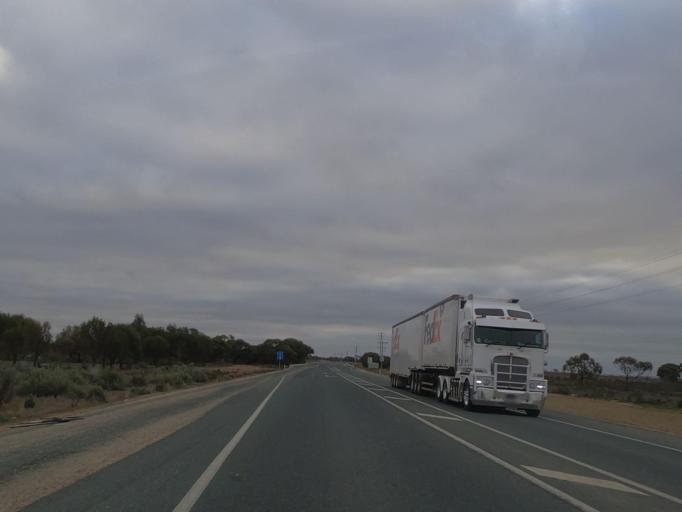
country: AU
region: Victoria
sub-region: Swan Hill
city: Swan Hill
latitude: -35.5461
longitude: 143.7609
